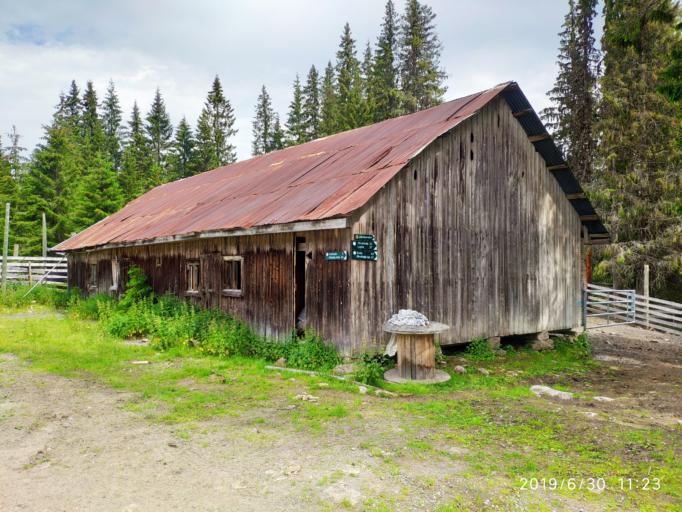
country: NO
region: Oppland
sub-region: Lunner
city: Grua
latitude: 60.2723
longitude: 10.7593
